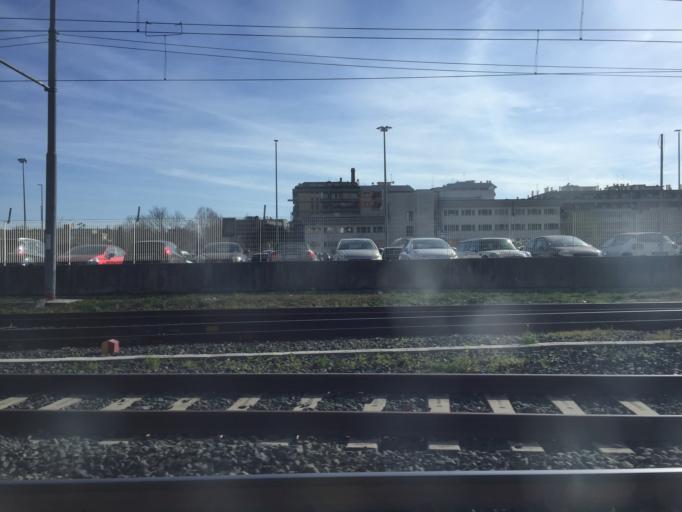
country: IT
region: Latium
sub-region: Citta metropolitana di Roma Capitale
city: Rome
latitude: 41.8713
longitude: 12.4889
